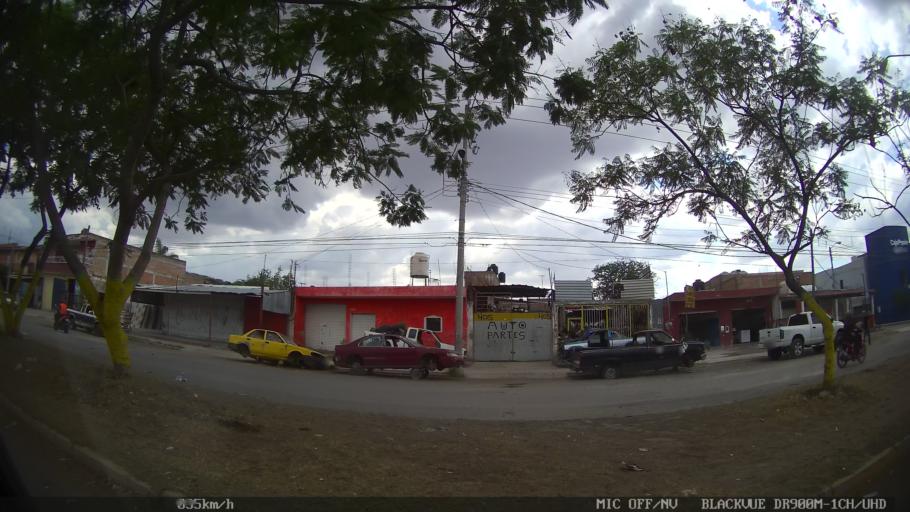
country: MX
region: Jalisco
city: Tlaquepaque
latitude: 20.6736
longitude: -103.2572
